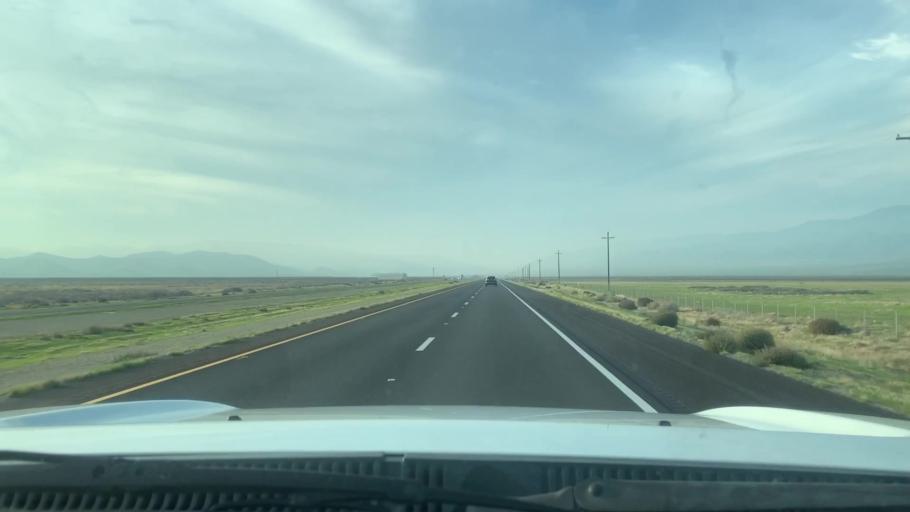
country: US
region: California
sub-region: San Luis Obispo County
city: Shandon
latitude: 35.6679
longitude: -120.0752
